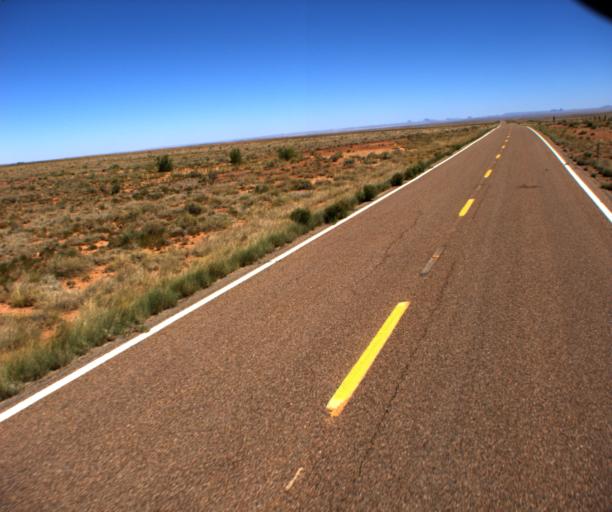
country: US
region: Arizona
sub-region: Navajo County
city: Winslow
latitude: 34.8677
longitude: -110.6580
